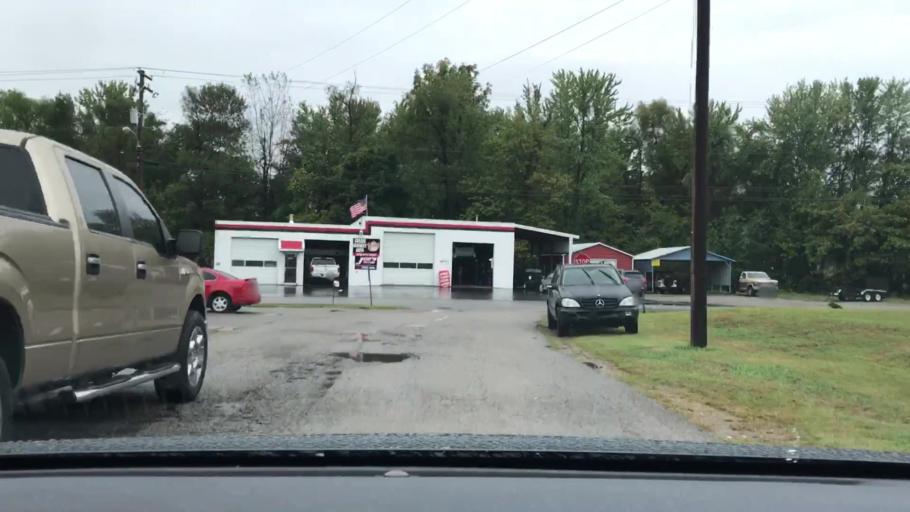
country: US
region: Kentucky
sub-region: McLean County
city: Calhoun
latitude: 37.5465
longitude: -87.2591
